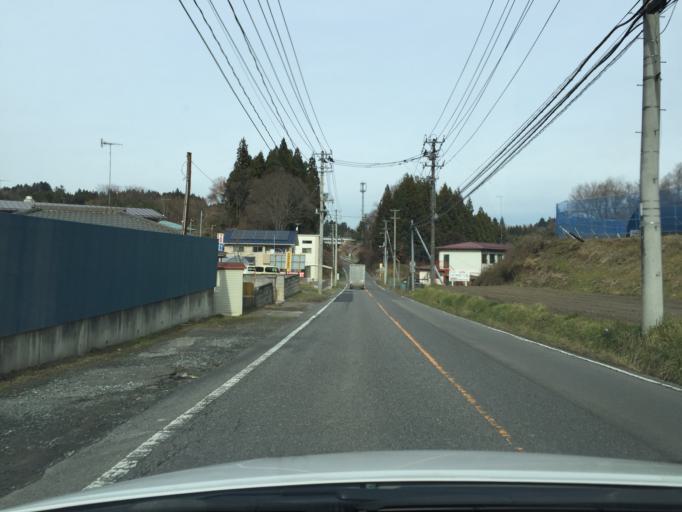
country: JP
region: Fukushima
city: Funehikimachi-funehiki
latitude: 37.2680
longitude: 140.6297
